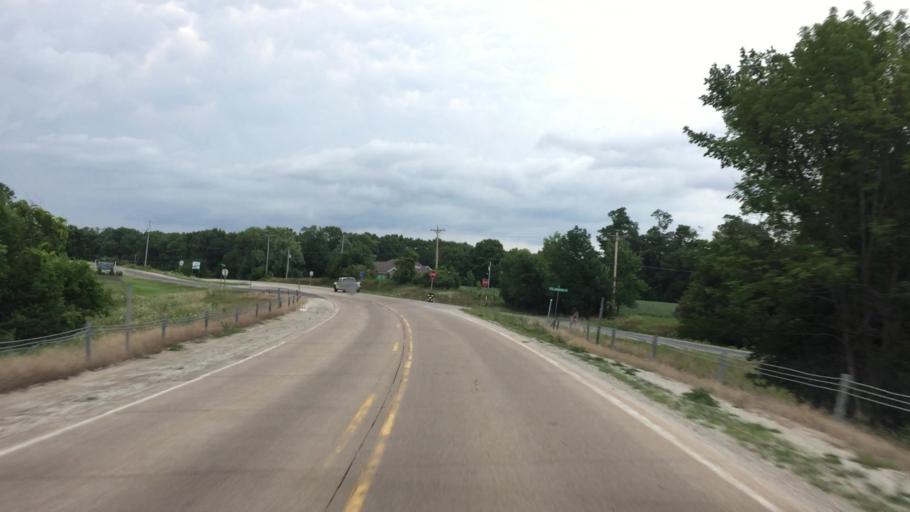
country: US
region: Iowa
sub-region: Lee County
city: Fort Madison
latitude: 40.6424
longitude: -91.3189
